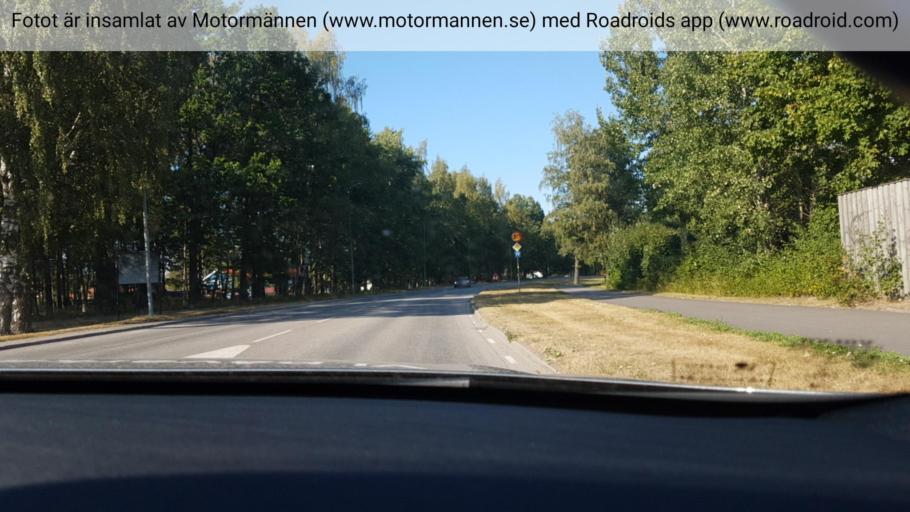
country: SE
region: Vaestra Goetaland
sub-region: Mariestads Kommun
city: Mariestad
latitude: 58.7028
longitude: 13.7989
